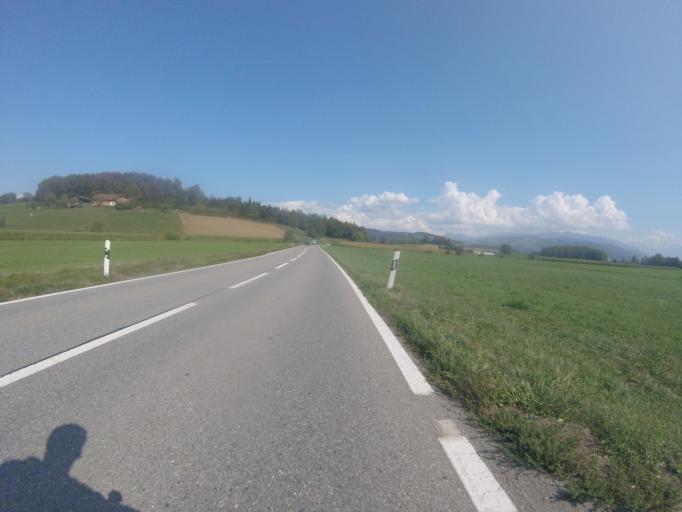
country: CH
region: Bern
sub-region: Thun District
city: Uttigen
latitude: 46.7888
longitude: 7.5620
